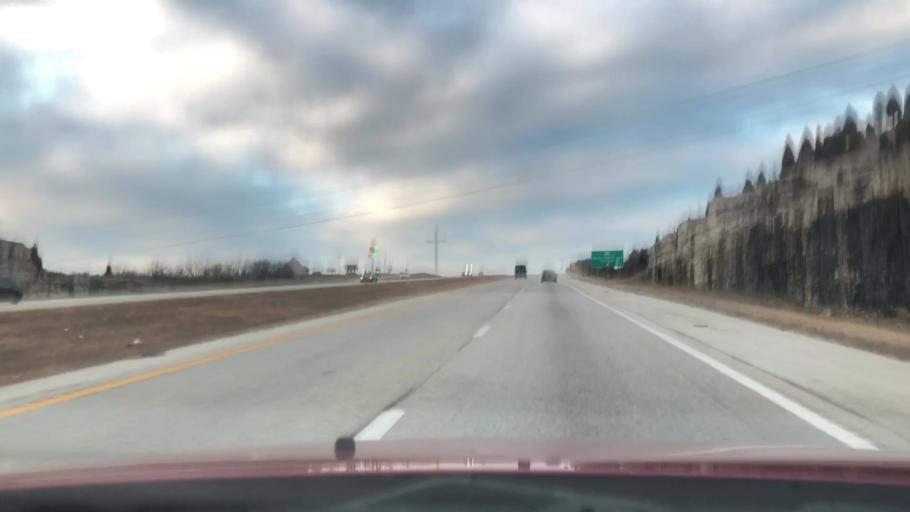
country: US
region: Missouri
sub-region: Taney County
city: Merriam Woods
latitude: 36.7424
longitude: -93.2219
